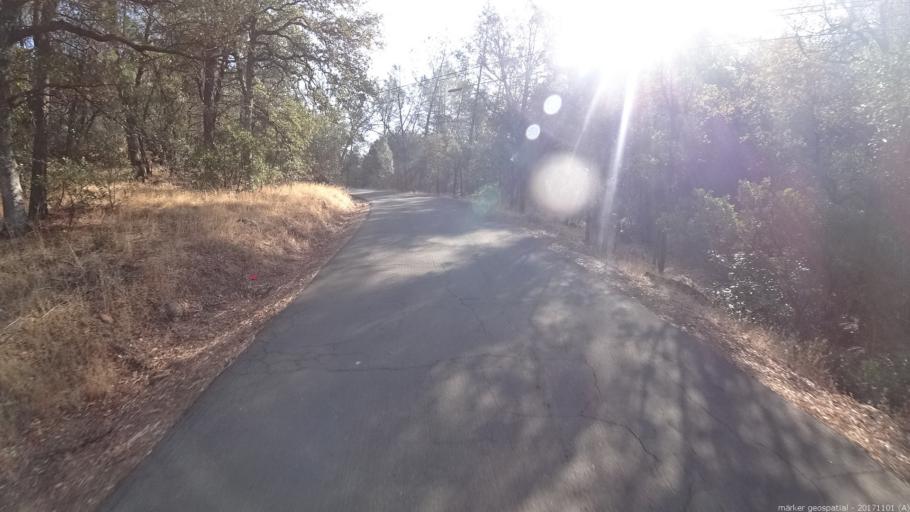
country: US
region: California
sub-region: Shasta County
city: Shasta Lake
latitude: 40.7080
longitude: -122.3223
